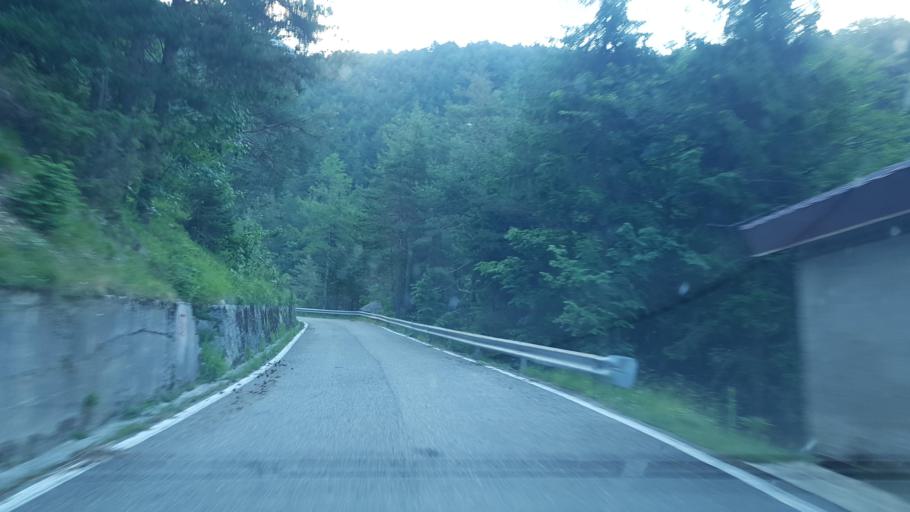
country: IT
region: Friuli Venezia Giulia
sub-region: Provincia di Udine
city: Dogna
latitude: 46.4599
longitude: 13.3775
